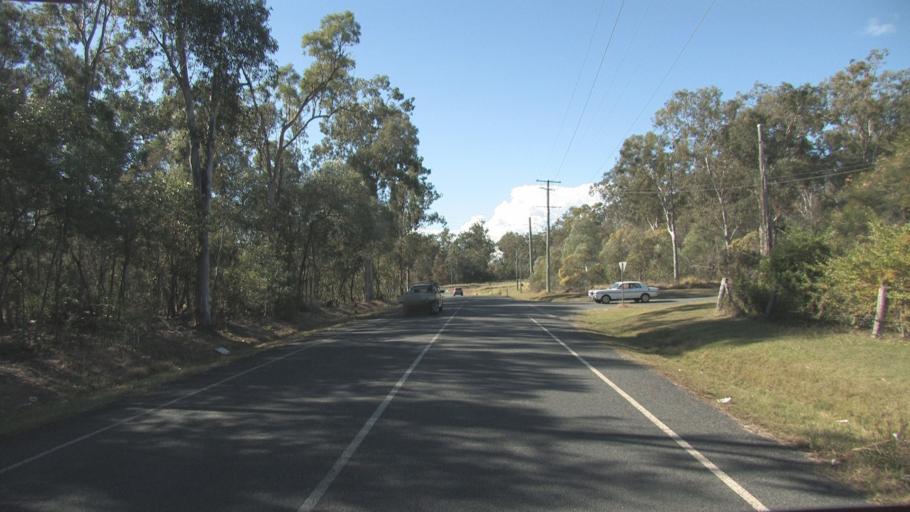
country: AU
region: Queensland
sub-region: Logan
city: North Maclean
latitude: -27.8077
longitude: 153.0599
